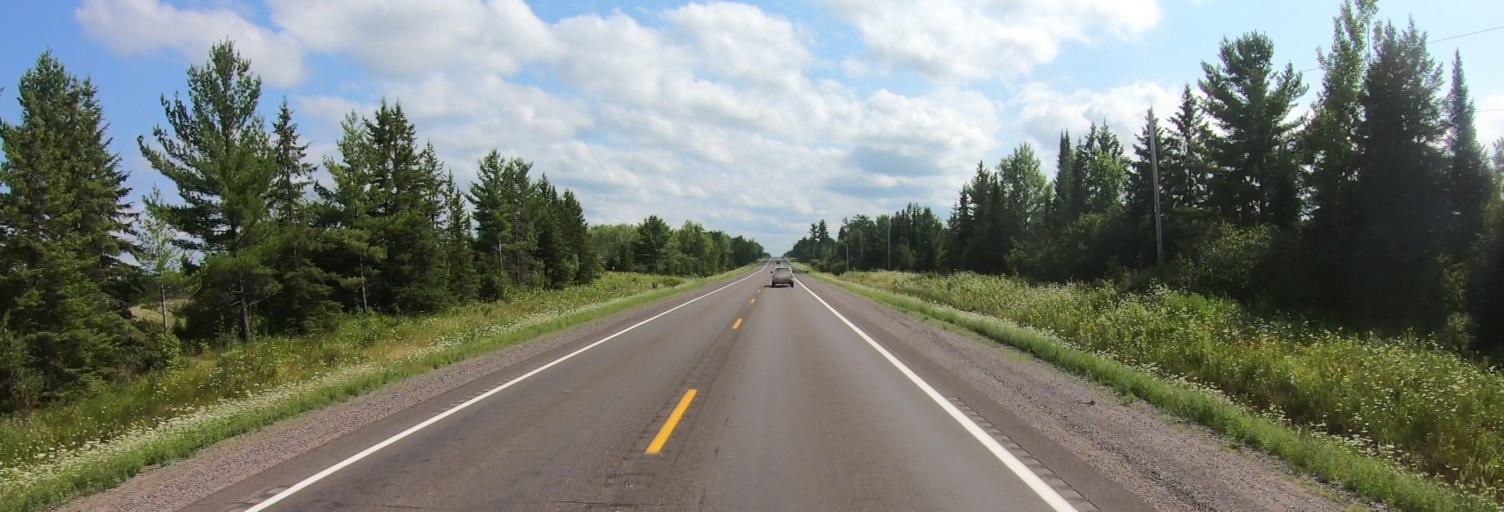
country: US
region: Michigan
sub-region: Ontonagon County
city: Ontonagon
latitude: 46.6162
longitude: -89.1788
